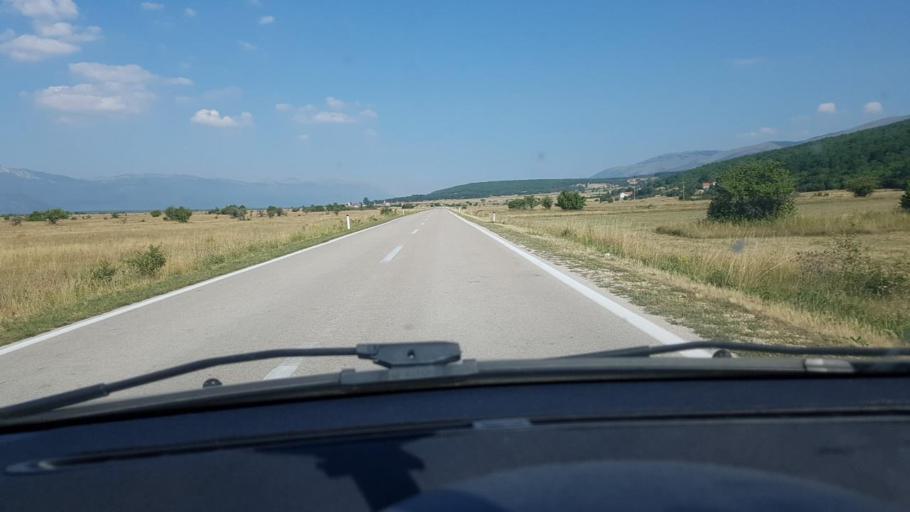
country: BA
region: Federation of Bosnia and Herzegovina
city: Glamoc
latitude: 43.9115
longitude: 16.7989
